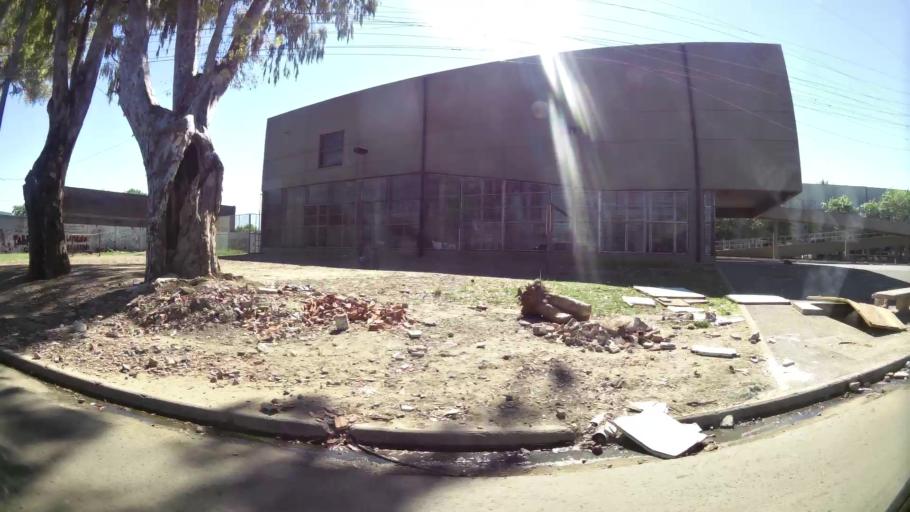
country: AR
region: Santa Fe
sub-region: Departamento de Rosario
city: Rosario
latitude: -32.9575
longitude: -60.6918
